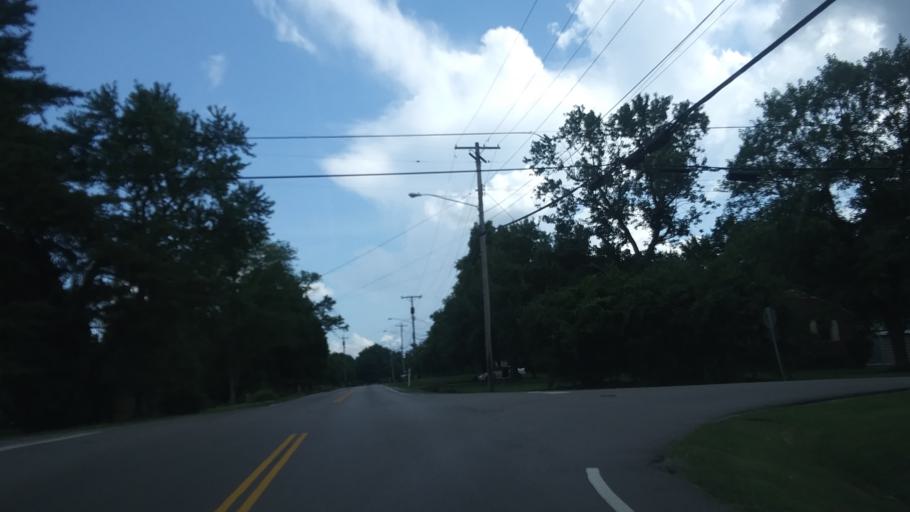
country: US
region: Tennessee
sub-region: Davidson County
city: Oak Hill
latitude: 36.0685
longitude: -86.6989
